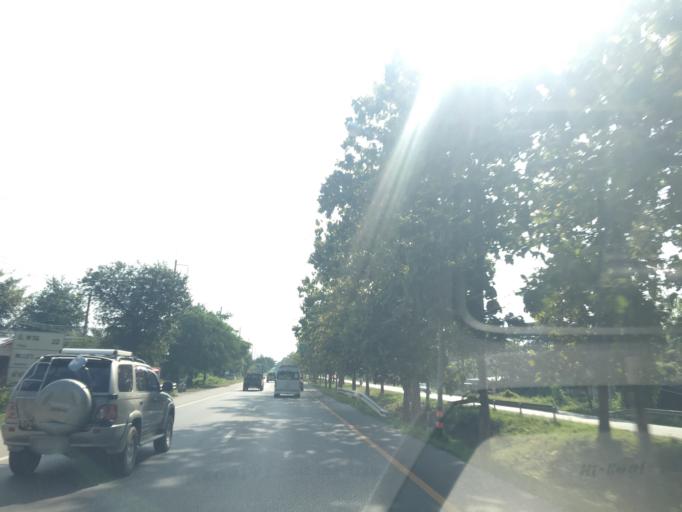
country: TH
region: Chiang Rai
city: Mae Lao
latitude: 19.7427
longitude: 99.7247
